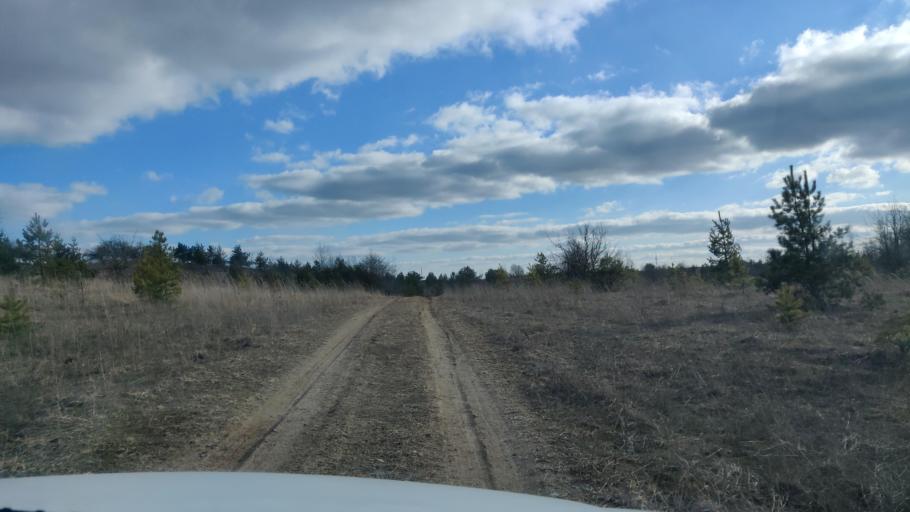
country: LT
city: Lentvaris
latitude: 54.6135
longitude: 24.9991
